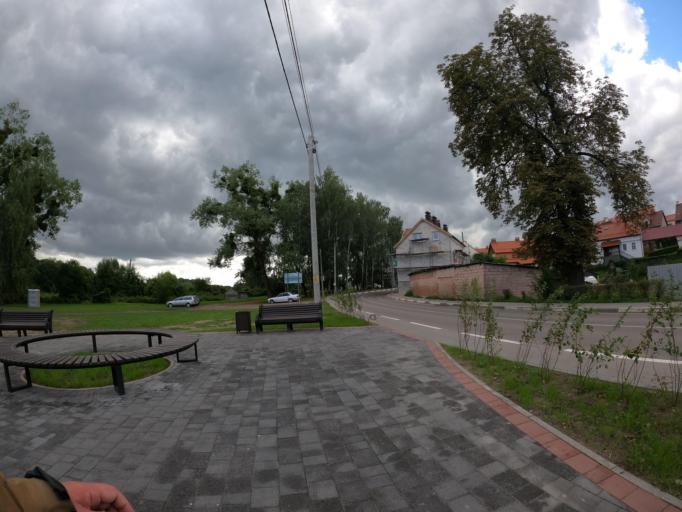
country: RU
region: Kaliningrad
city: Zheleznodorozhnyy
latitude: 54.3628
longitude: 21.3072
